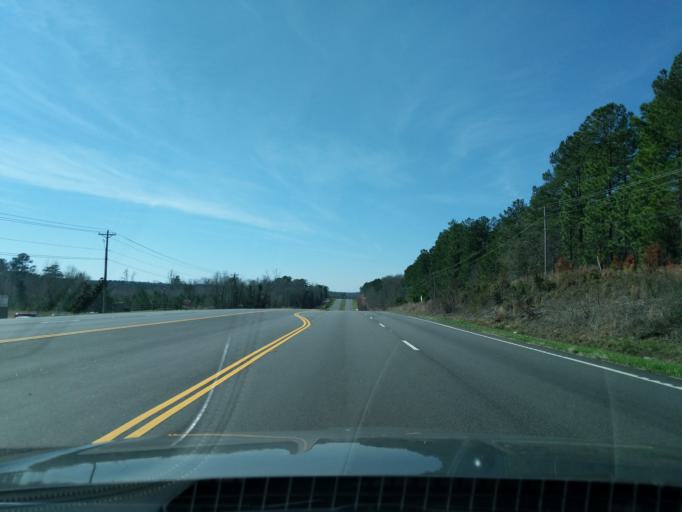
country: US
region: South Carolina
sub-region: Aiken County
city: Burnettown
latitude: 33.5203
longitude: -81.8562
